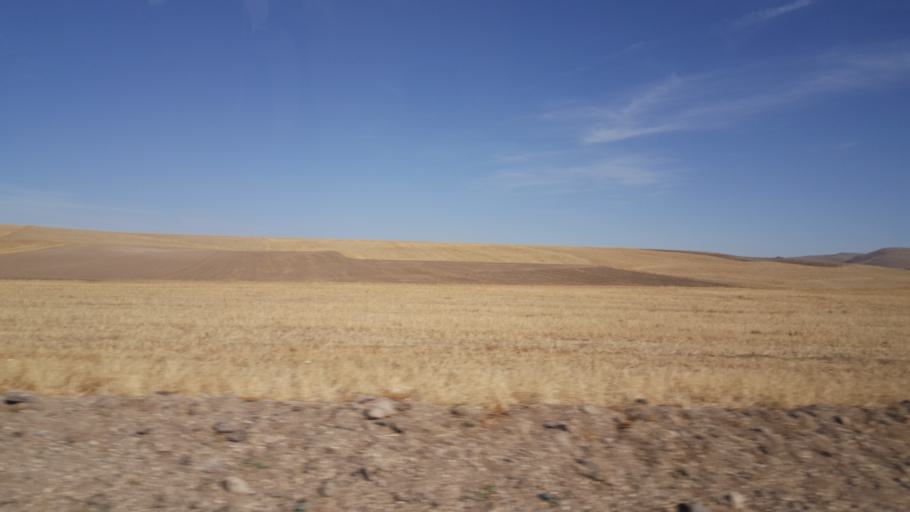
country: TR
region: Ankara
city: Yenice
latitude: 39.3178
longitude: 32.7562
